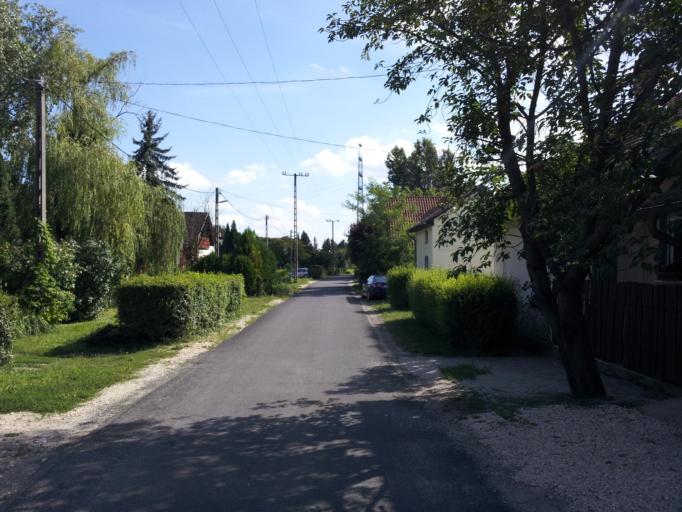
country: HU
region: Pest
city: Szigetcsep
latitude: 47.2580
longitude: 18.9869
